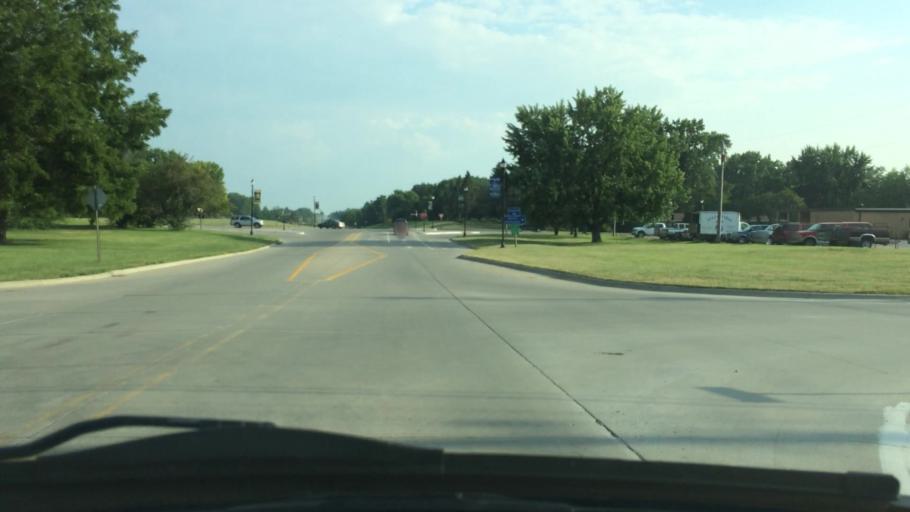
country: US
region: Iowa
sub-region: Henry County
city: Mount Pleasant
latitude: 40.9653
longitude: -91.5392
